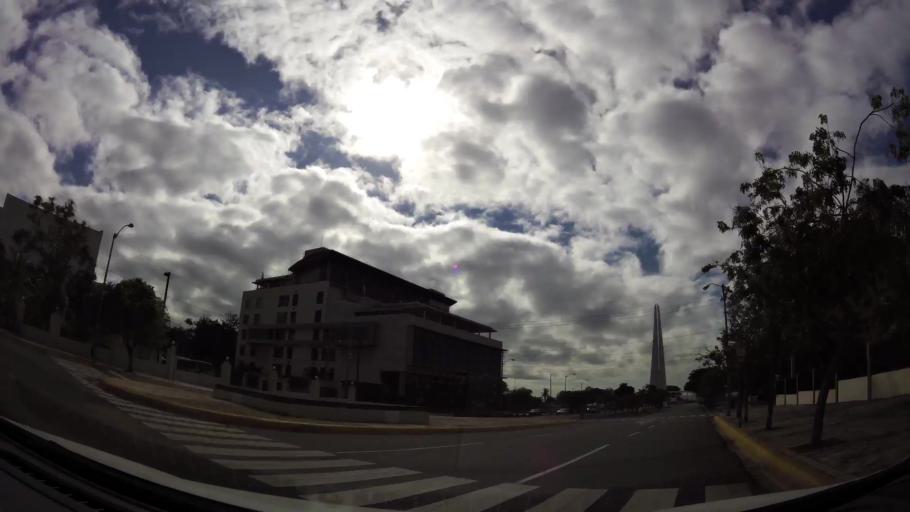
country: DO
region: Nacional
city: La Julia
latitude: 18.4483
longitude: -69.9261
